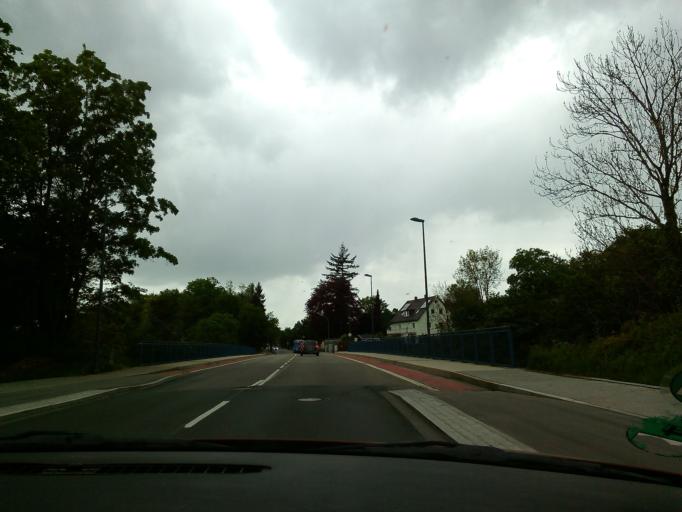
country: DE
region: Bavaria
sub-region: Upper Bavaria
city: Grafelfing
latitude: 48.1269
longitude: 11.4373
